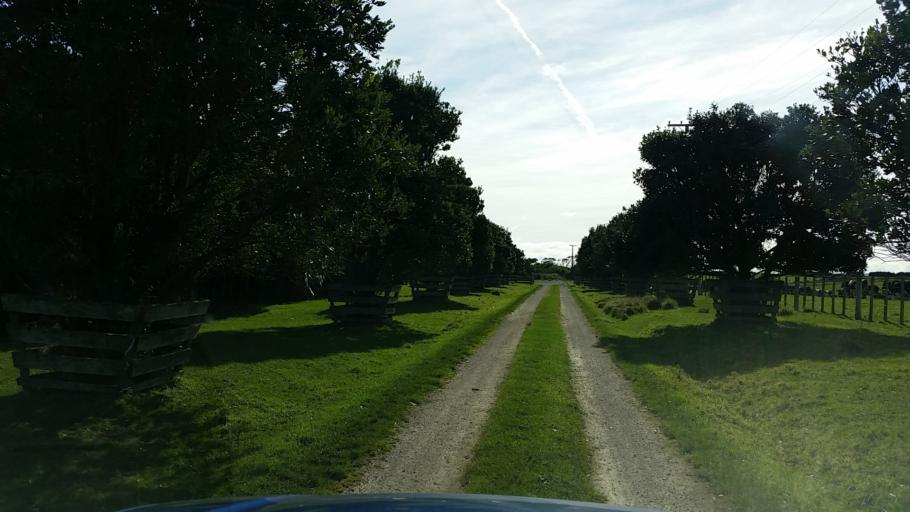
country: NZ
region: Taranaki
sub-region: South Taranaki District
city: Patea
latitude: -39.7676
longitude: 174.4932
